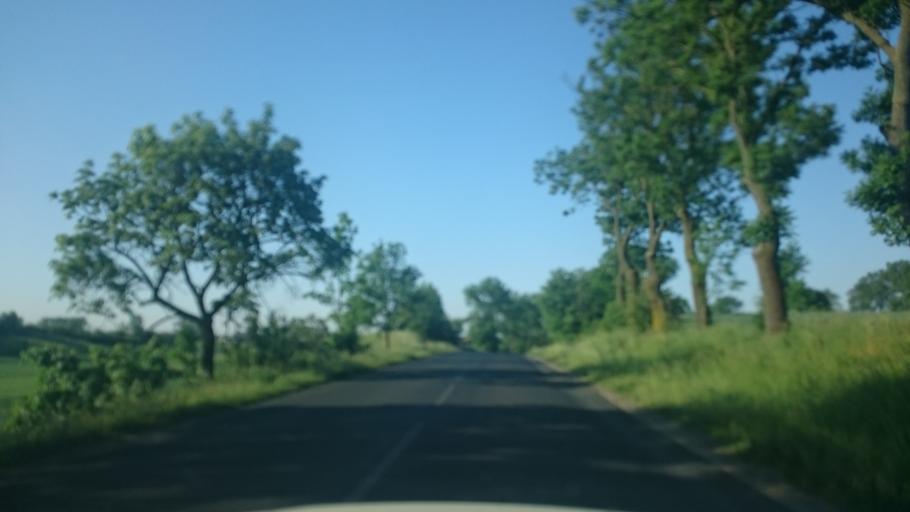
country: PL
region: Kujawsko-Pomorskie
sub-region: Powiat golubsko-dobrzynski
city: Zbojno
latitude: 52.9844
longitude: 19.1194
